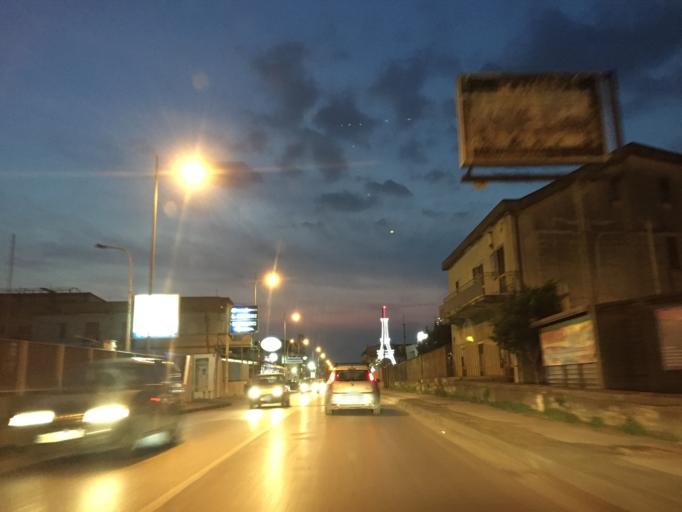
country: IT
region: Campania
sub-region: Provincia di Salerno
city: San Lorenzo
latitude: 40.7479
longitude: 14.5960
